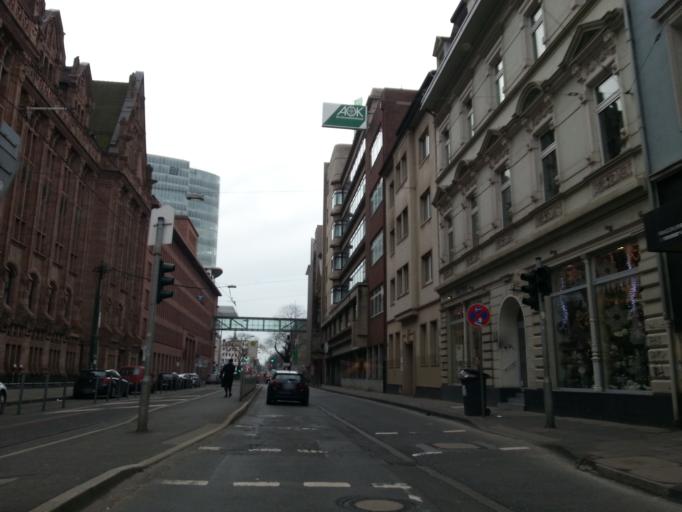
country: DE
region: North Rhine-Westphalia
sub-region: Regierungsbezirk Dusseldorf
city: Dusseldorf
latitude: 51.2216
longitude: 6.7753
